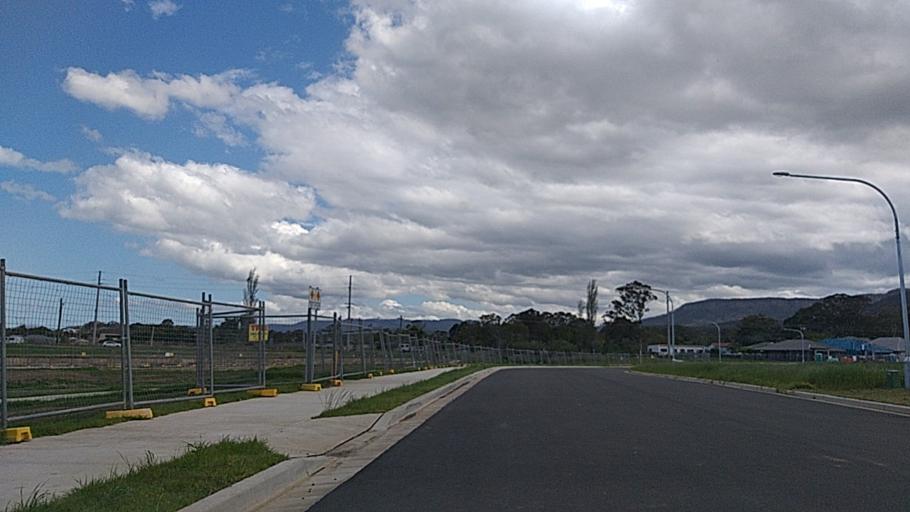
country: AU
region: New South Wales
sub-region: Wollongong
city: Dapto
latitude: -34.4771
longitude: 150.7666
